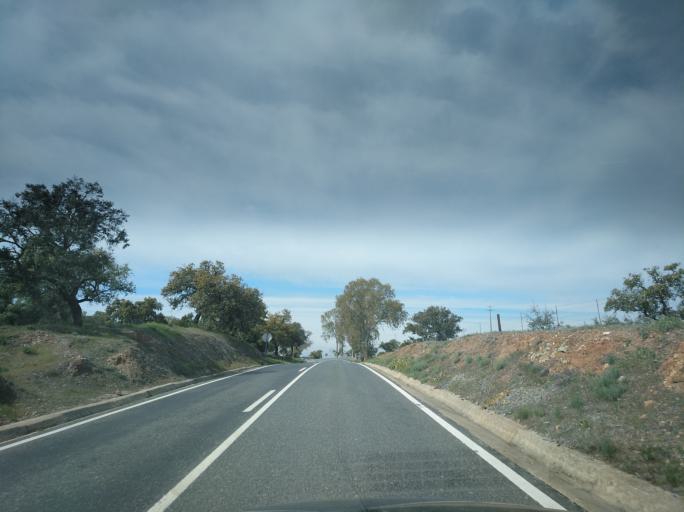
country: PT
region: Beja
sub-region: Mertola
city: Mertola
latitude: 37.7356
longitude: -7.7728
